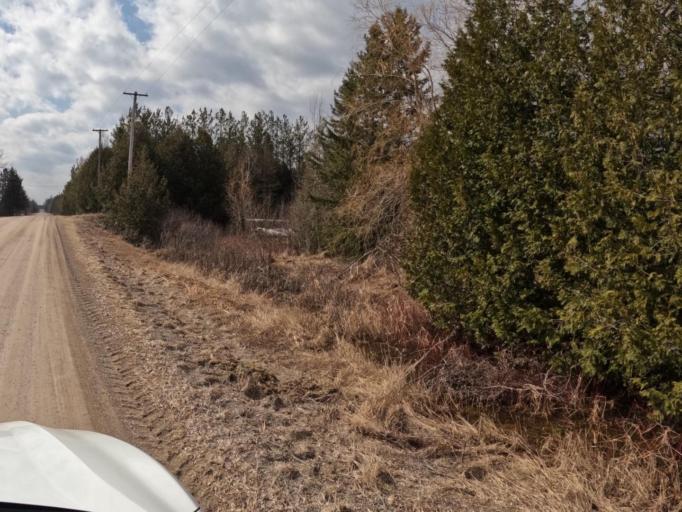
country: CA
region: Ontario
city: Orangeville
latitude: 43.9033
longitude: -80.2359
